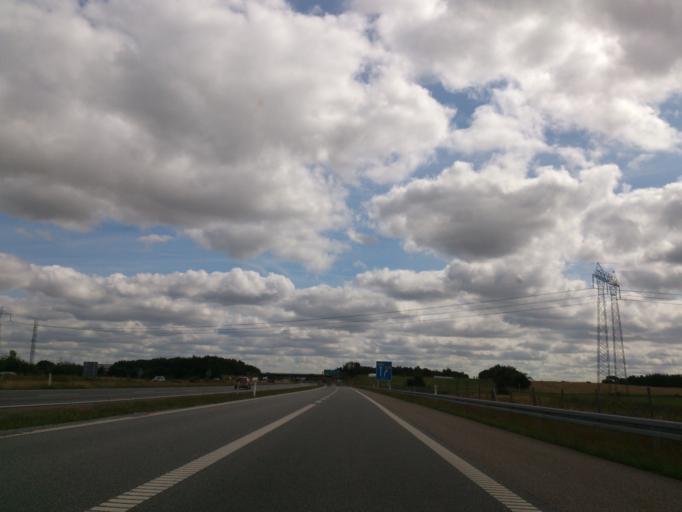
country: DK
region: South Denmark
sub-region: Aabenraa Kommune
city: Krusa
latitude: 54.9445
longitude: 9.3833
